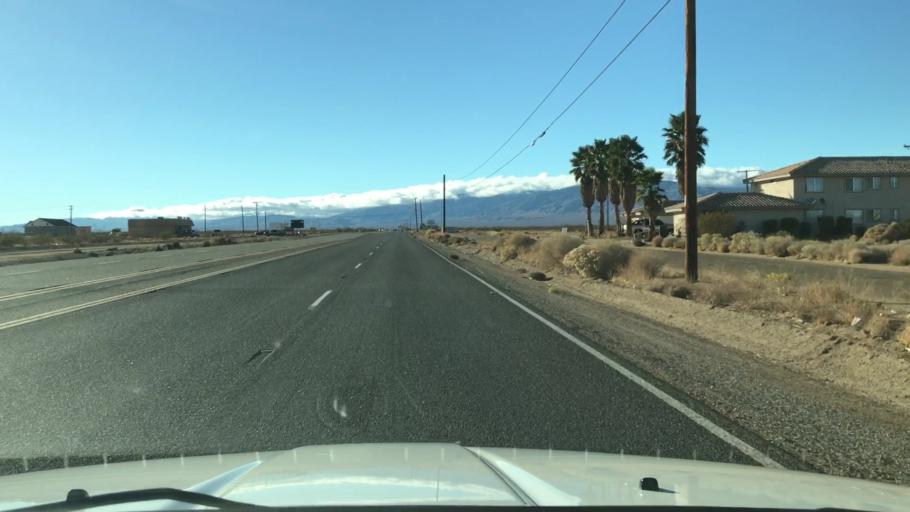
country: US
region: California
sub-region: Kern County
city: California City
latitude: 35.1258
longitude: -118.0096
